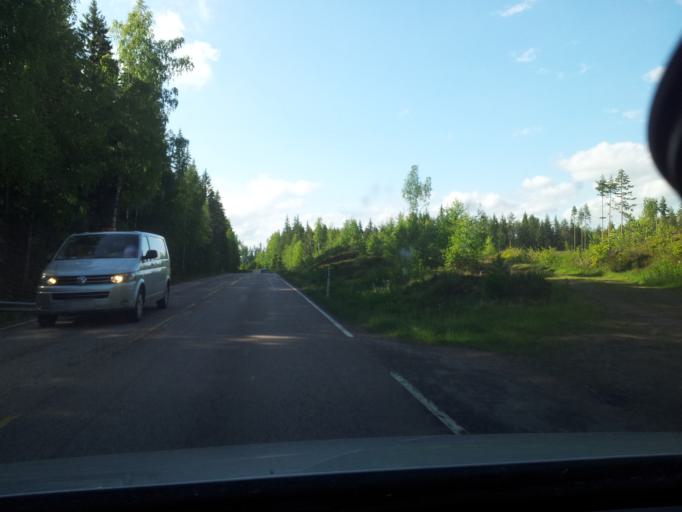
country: FI
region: South Karelia
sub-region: Lappeenranta
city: Luumaeki
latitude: 60.9734
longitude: 27.5562
